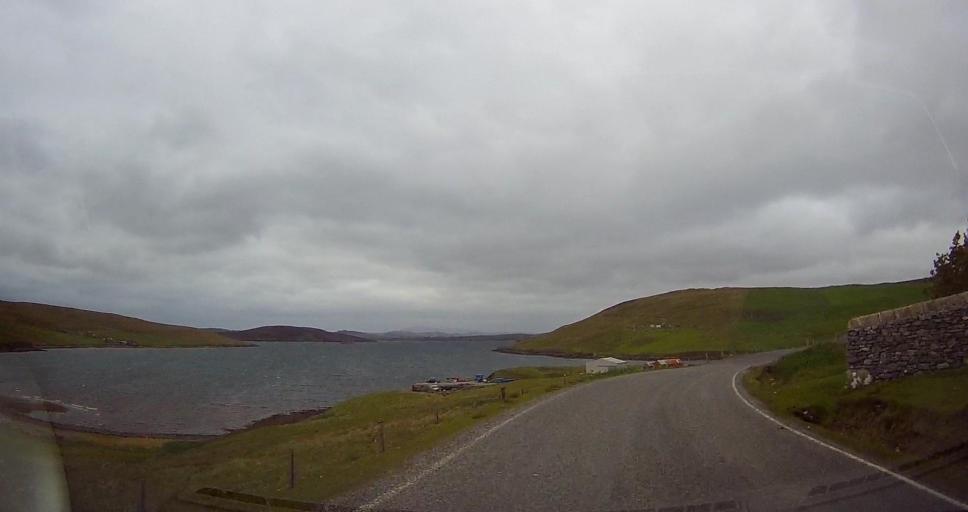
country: GB
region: Scotland
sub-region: Shetland Islands
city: Lerwick
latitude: 60.3336
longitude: -1.3353
